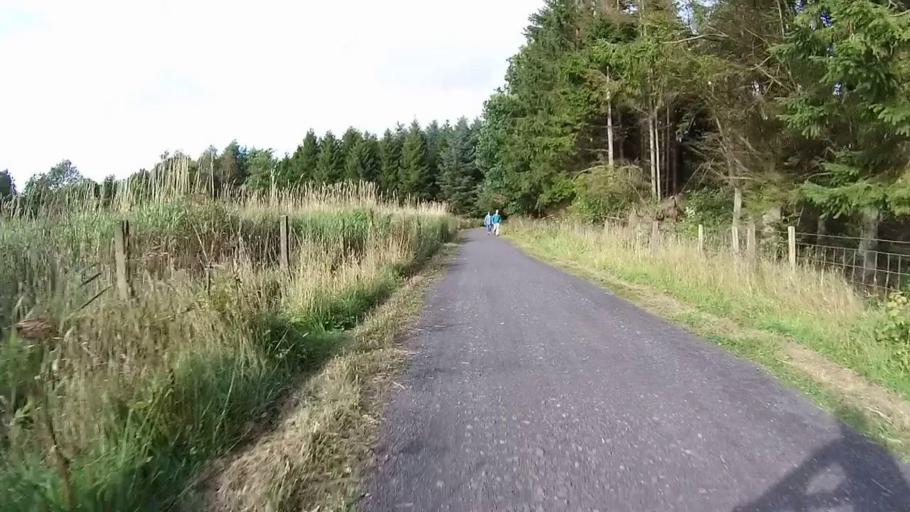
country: GB
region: Scotland
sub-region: Perth and Kinross
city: Kinross
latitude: 56.2104
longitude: -3.4052
